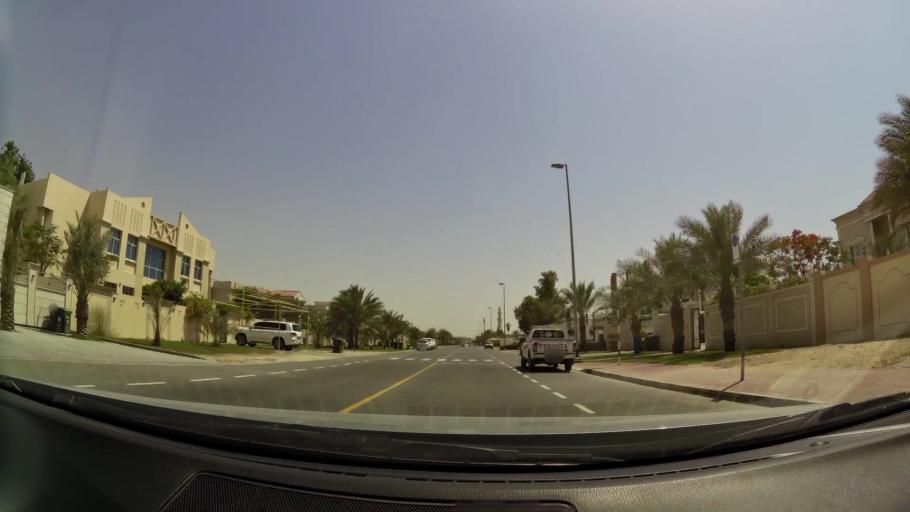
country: AE
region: Dubai
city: Dubai
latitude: 25.1108
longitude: 55.2153
